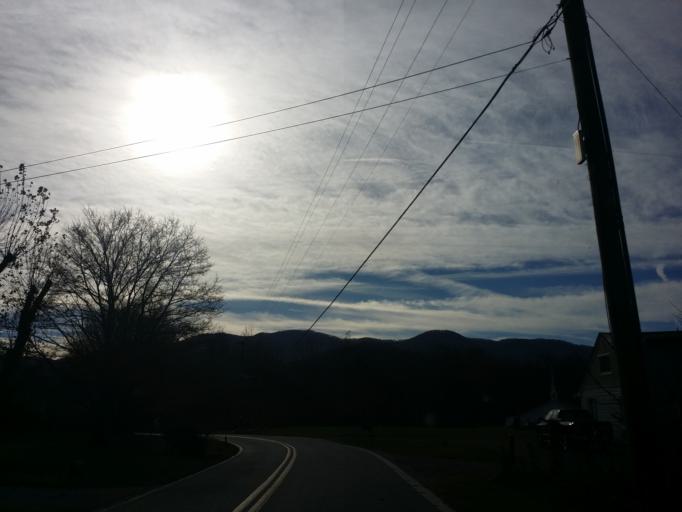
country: US
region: North Carolina
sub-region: Buncombe County
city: Swannanoa
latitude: 35.6141
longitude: -82.4254
